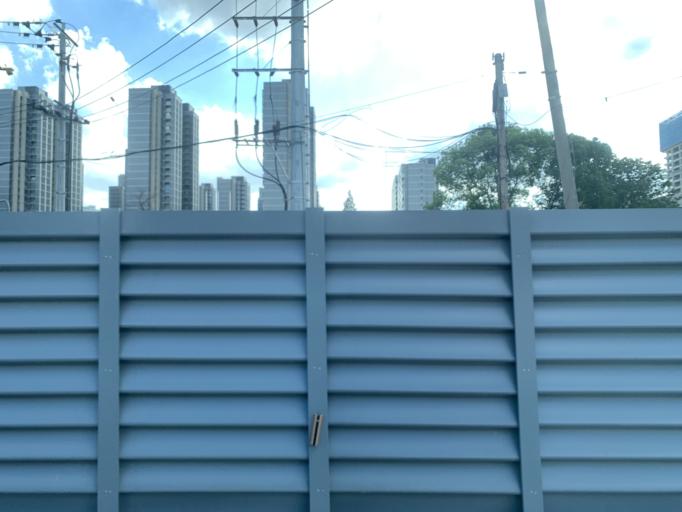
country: CN
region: Shanghai Shi
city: Pudong
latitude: 31.2439
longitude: 121.5374
